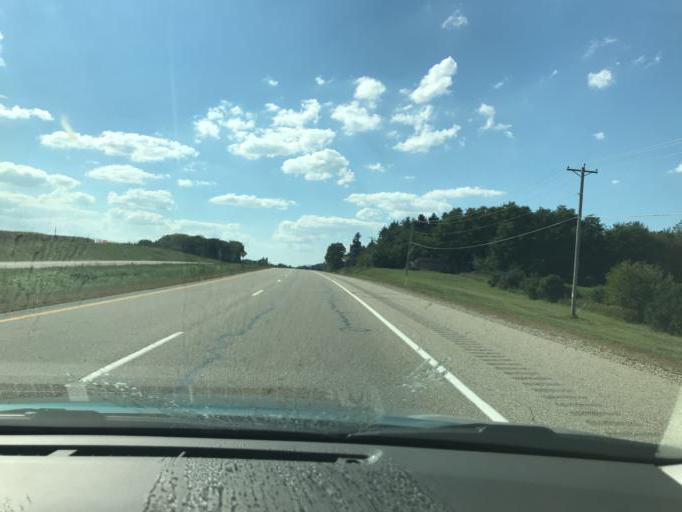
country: US
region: Wisconsin
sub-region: Walworth County
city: Lake Geneva
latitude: 42.5956
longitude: -88.3984
